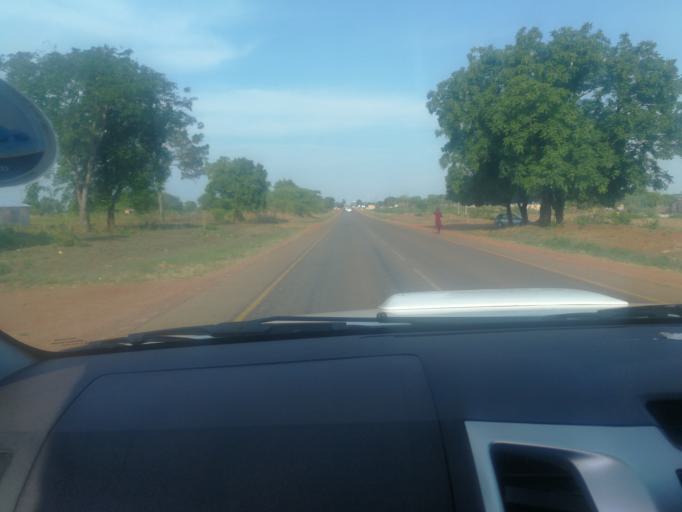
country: ZM
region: Northern
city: Kasama
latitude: -10.2169
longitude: 31.1461
